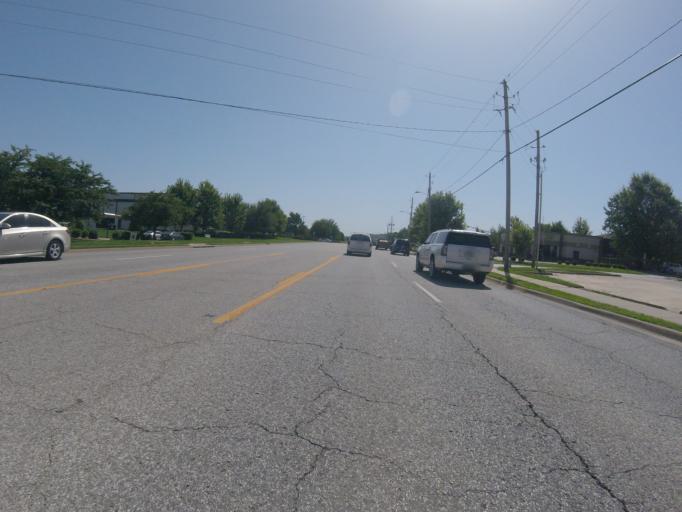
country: US
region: Arkansas
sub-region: Washington County
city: Fayetteville
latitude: 36.0784
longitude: -94.2064
